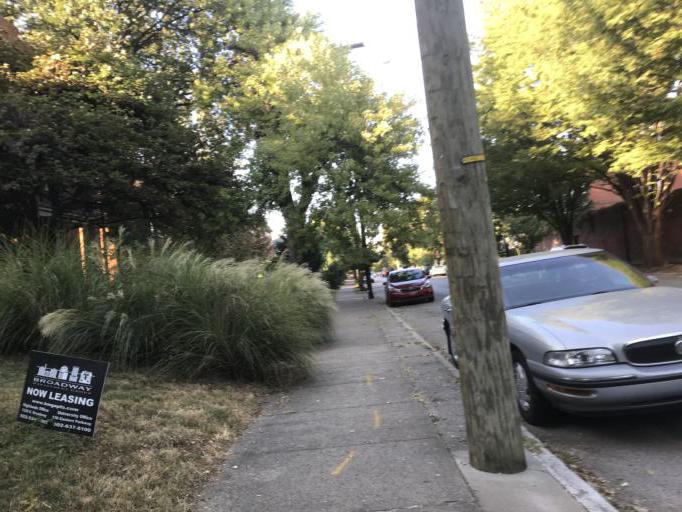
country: US
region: Kentucky
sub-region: Jefferson County
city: Louisville
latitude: 38.2320
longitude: -85.7644
